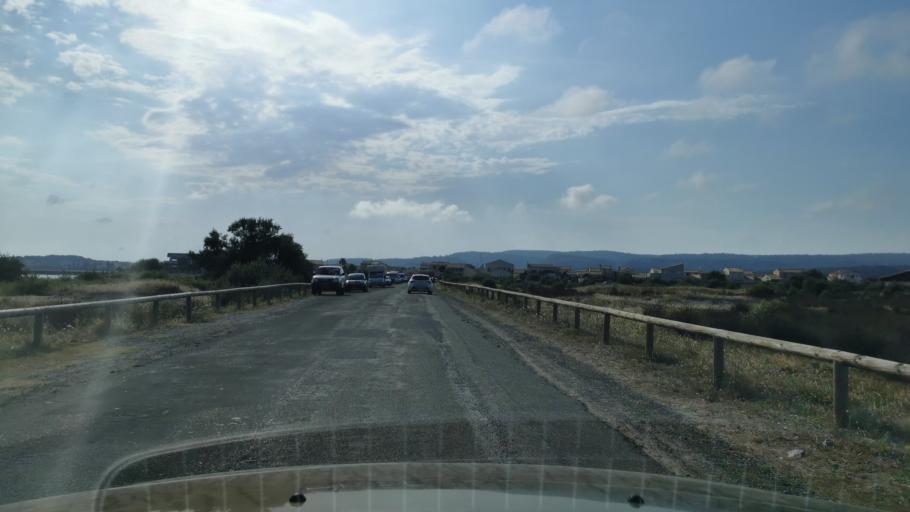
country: FR
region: Languedoc-Roussillon
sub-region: Departement de l'Aude
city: Gruissan
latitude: 43.1138
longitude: 3.1226
